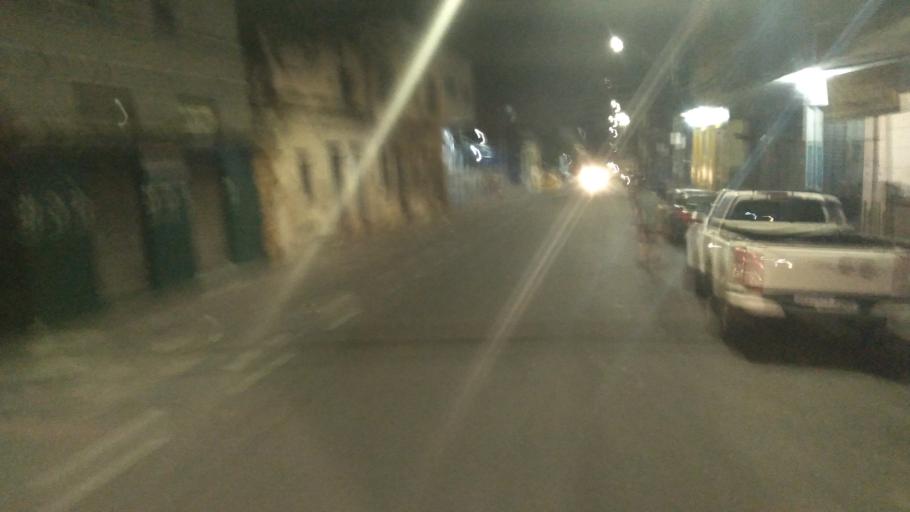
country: BR
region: Minas Gerais
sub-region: Belo Horizonte
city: Belo Horizonte
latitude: -19.9091
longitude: -43.9434
